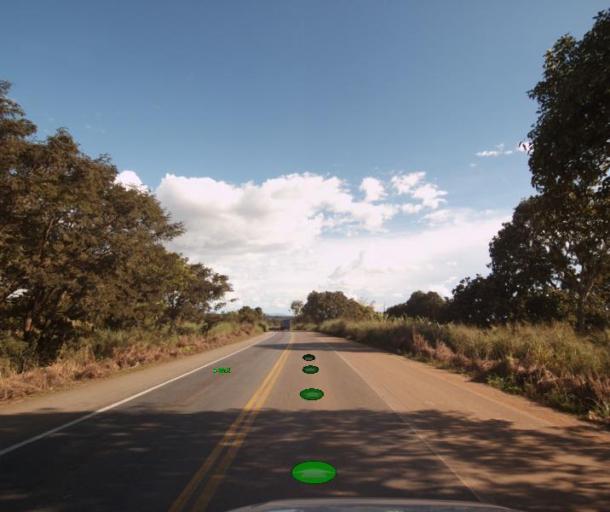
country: BR
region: Goias
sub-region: Porangatu
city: Porangatu
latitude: -13.1100
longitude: -49.2019
